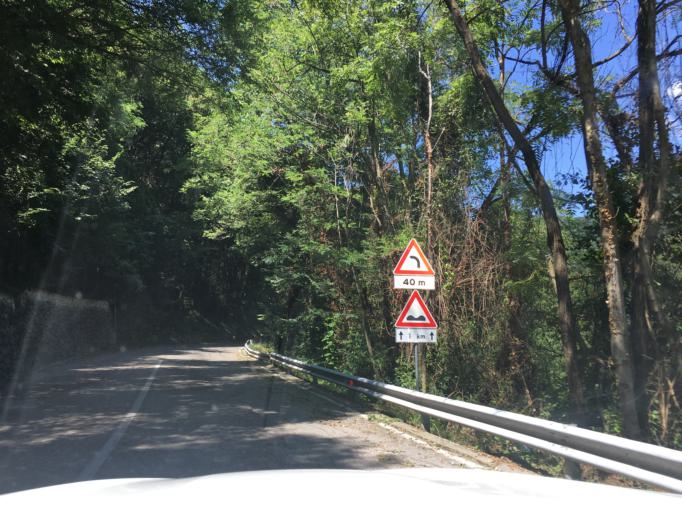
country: IT
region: Lombardy
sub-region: Provincia di Bergamo
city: Nembro
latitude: 45.7596
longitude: 9.7519
